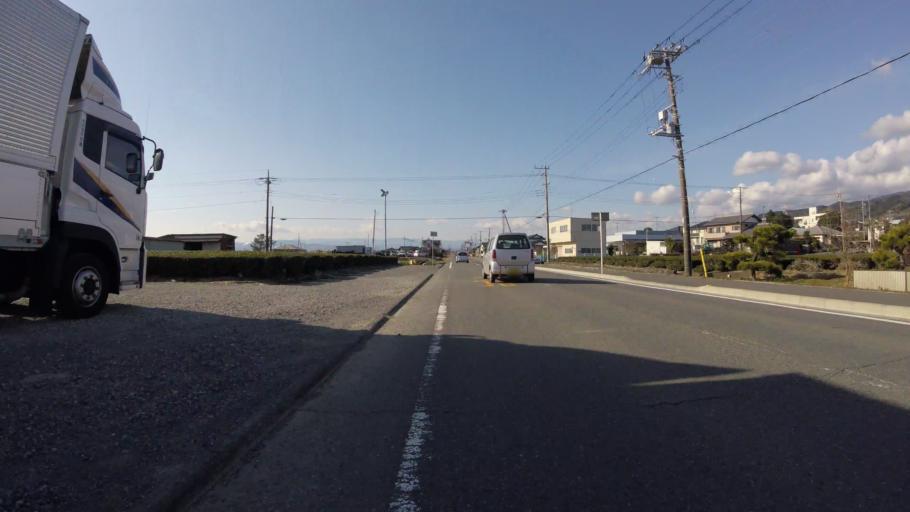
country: JP
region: Shizuoka
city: Fuji
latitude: 35.1479
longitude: 138.7716
